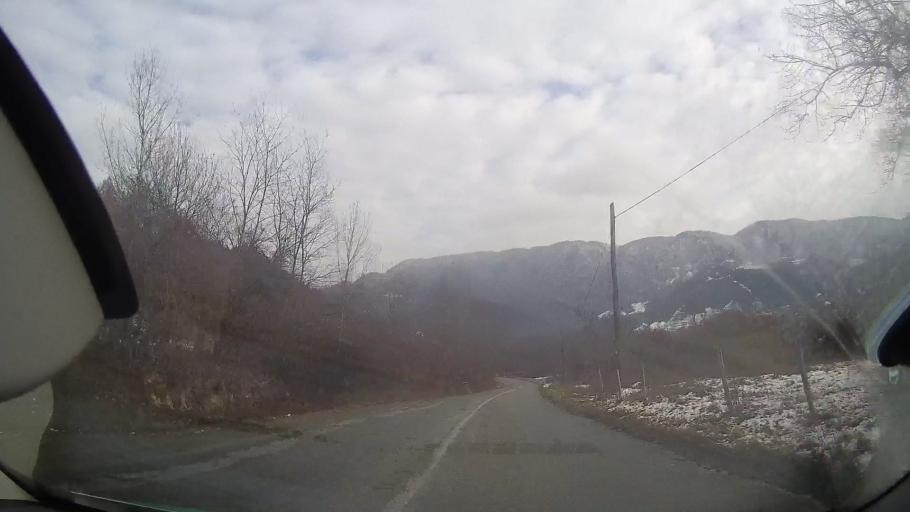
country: RO
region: Alba
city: Salciua de Sus
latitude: 46.4037
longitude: 23.4343
